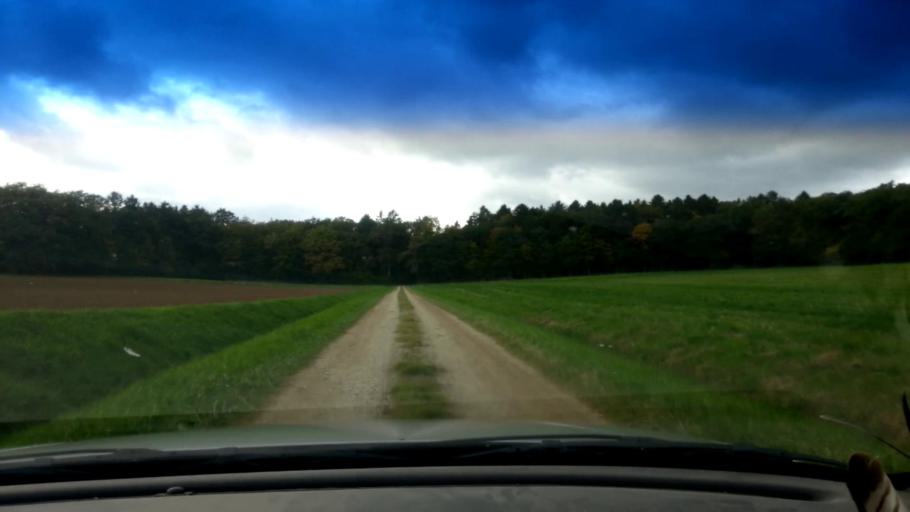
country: DE
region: Bavaria
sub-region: Upper Franconia
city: Zapfendorf
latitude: 49.9955
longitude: 10.9807
